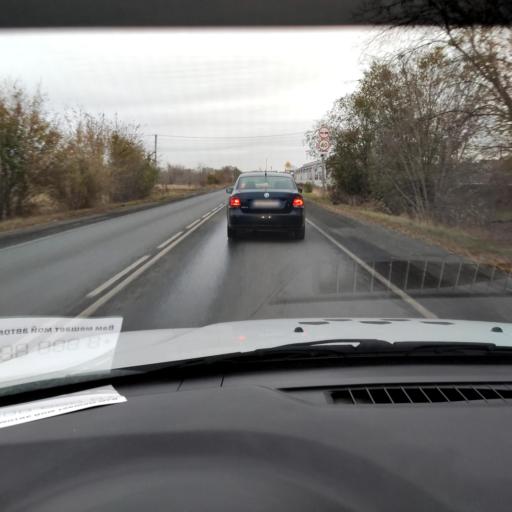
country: RU
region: Samara
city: Podstepki
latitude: 53.5175
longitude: 49.2316
